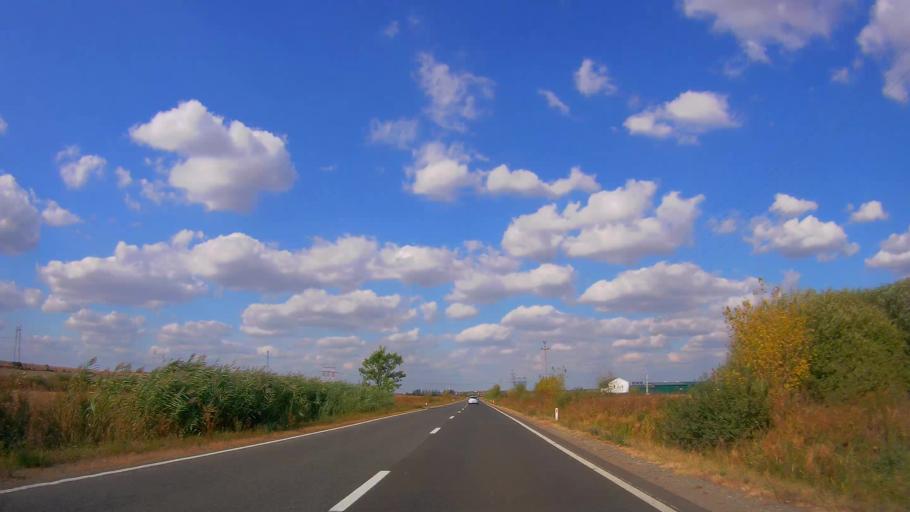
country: RO
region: Satu Mare
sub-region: Oras Ardud
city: Ardud
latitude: 47.6028
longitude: 22.8789
